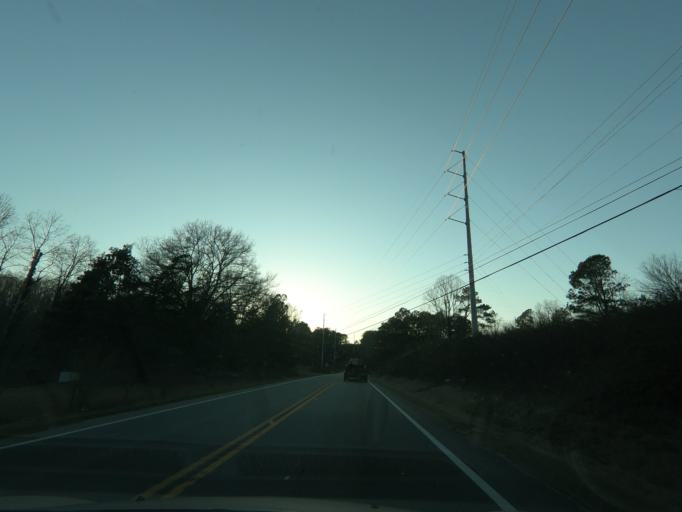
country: US
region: Georgia
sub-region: Forsyth County
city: Cumming
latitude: 34.3025
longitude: -84.1920
